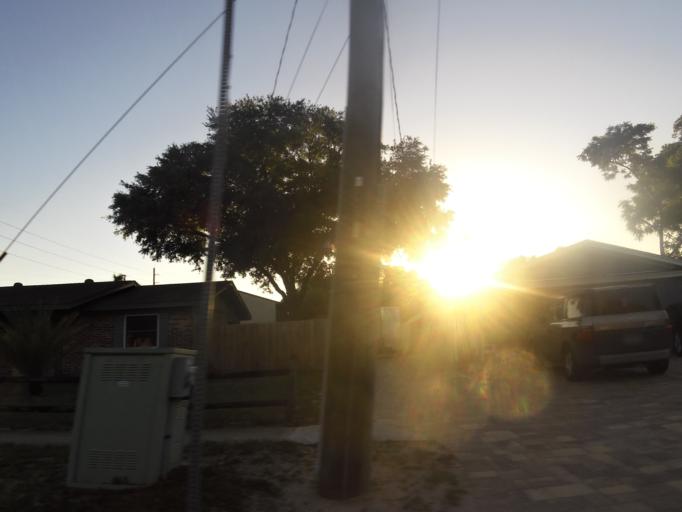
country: US
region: Florida
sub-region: Duval County
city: Jacksonville
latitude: 30.3459
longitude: -81.5687
